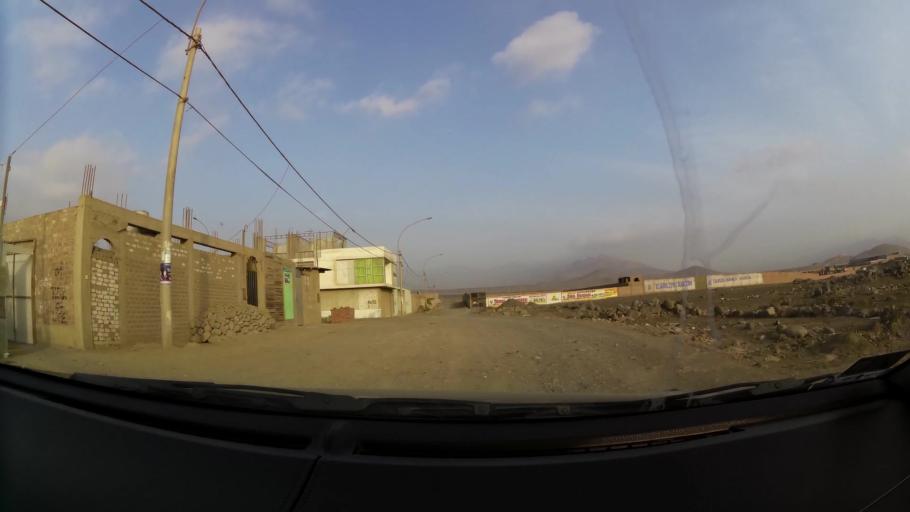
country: PE
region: Lima
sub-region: Lima
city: Santa Rosa
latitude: -11.7438
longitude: -77.1456
